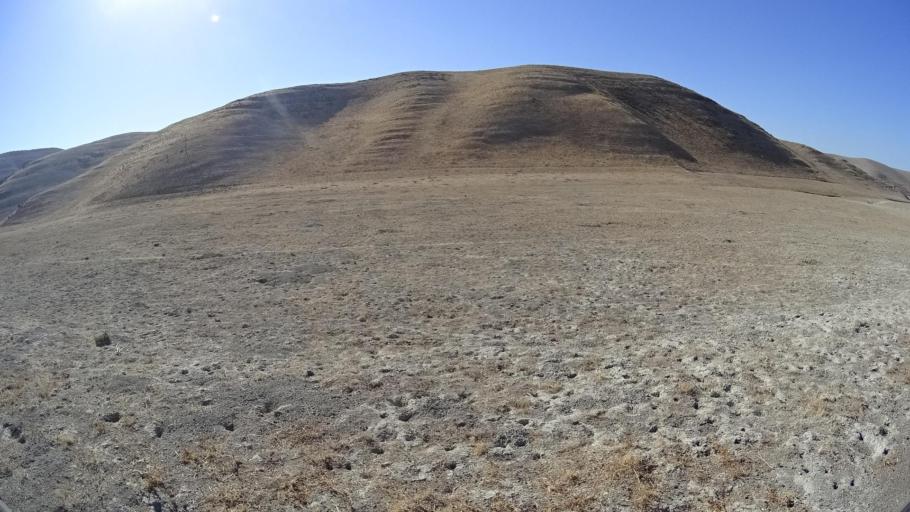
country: US
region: California
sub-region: Monterey County
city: King City
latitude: 36.1999
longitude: -120.9474
